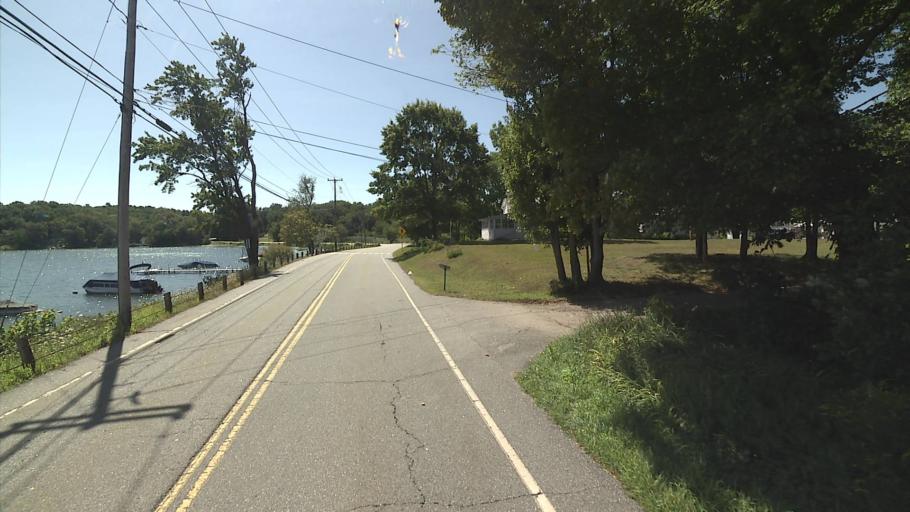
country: US
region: Connecticut
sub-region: Litchfield County
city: Bethlehem Village
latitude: 41.6890
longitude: -73.2324
